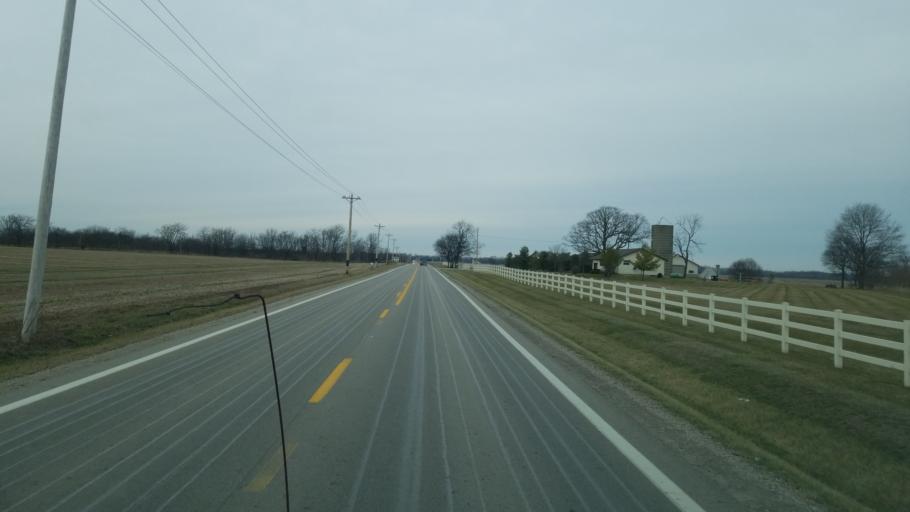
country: US
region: Ohio
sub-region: Pickaway County
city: Circleville
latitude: 39.5985
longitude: -83.0035
